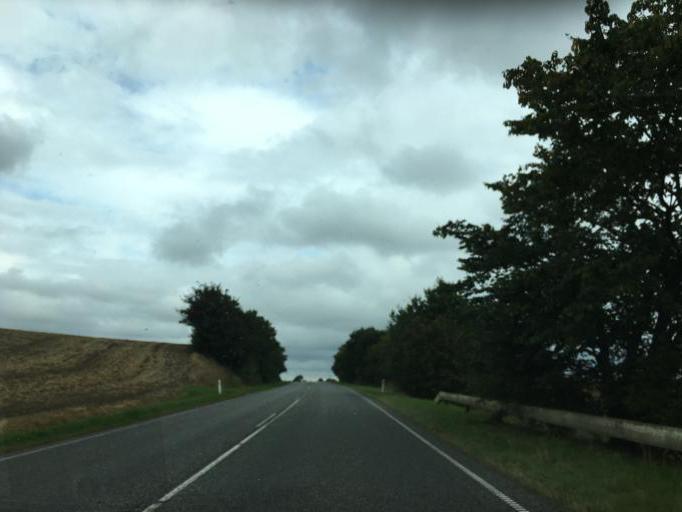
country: DK
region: South Denmark
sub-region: Kolding Kommune
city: Kolding
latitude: 55.5827
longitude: 9.4985
